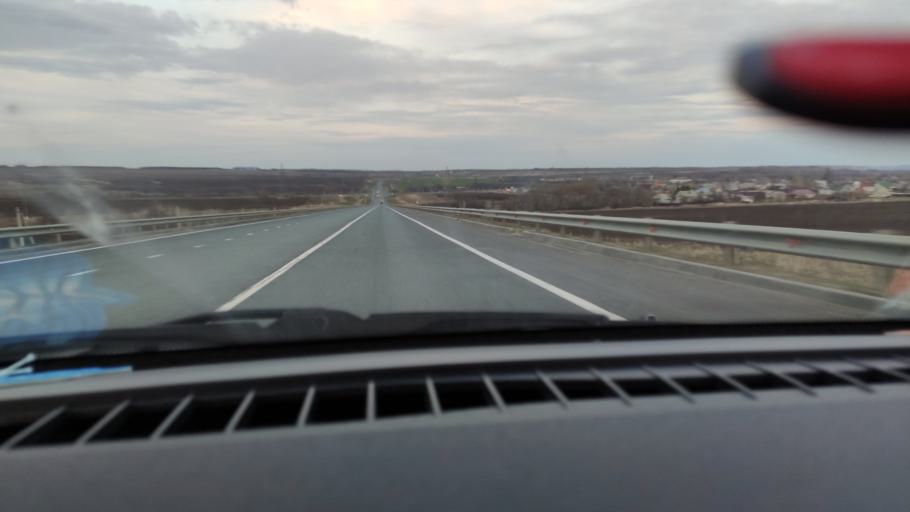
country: RU
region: Saratov
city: Yelshanka
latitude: 51.8239
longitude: 46.3826
